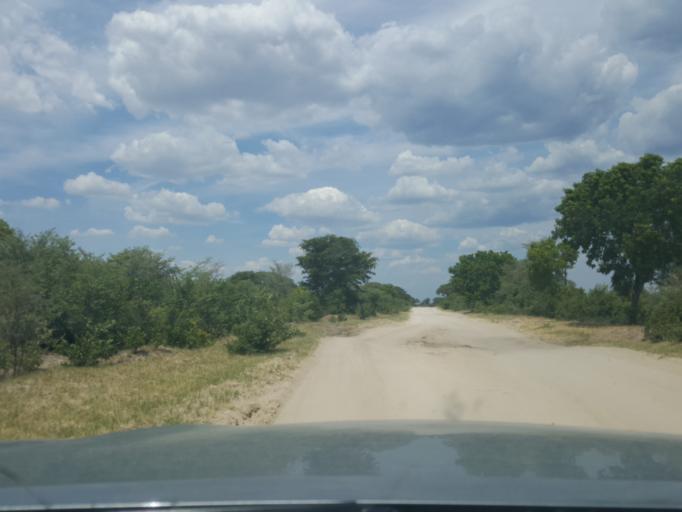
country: BW
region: North West
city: Shakawe
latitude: -18.4790
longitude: 22.1127
